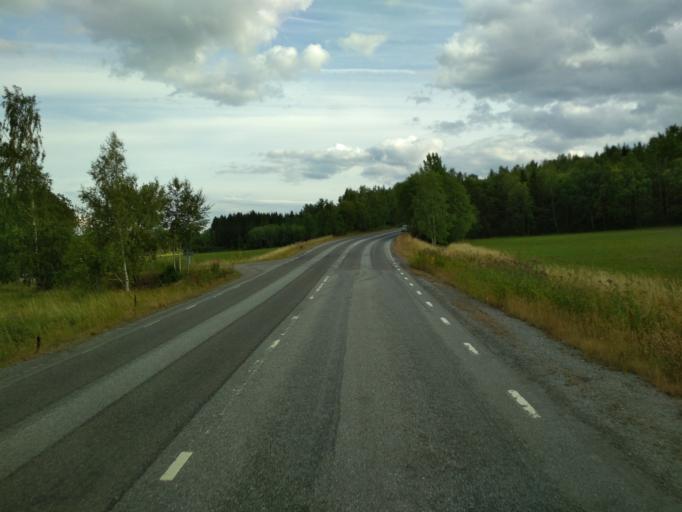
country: SE
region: Uppsala
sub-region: Habo Kommun
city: Balsta
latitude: 59.6548
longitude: 17.5574
